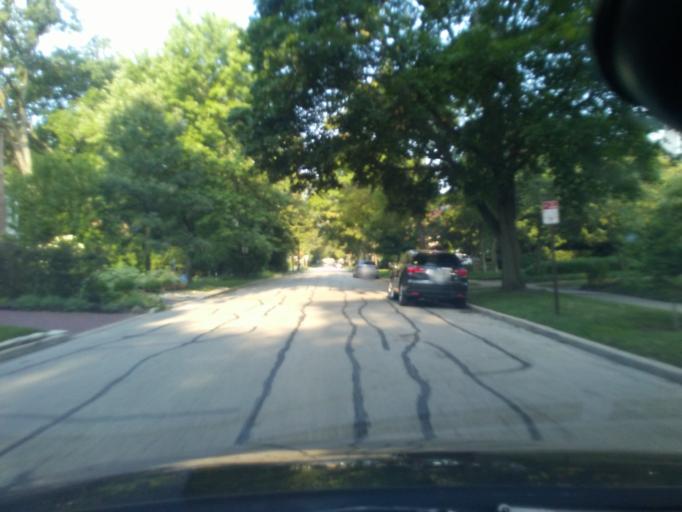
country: US
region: Illinois
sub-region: Cook County
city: Evanston
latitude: 42.0411
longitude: -87.6733
